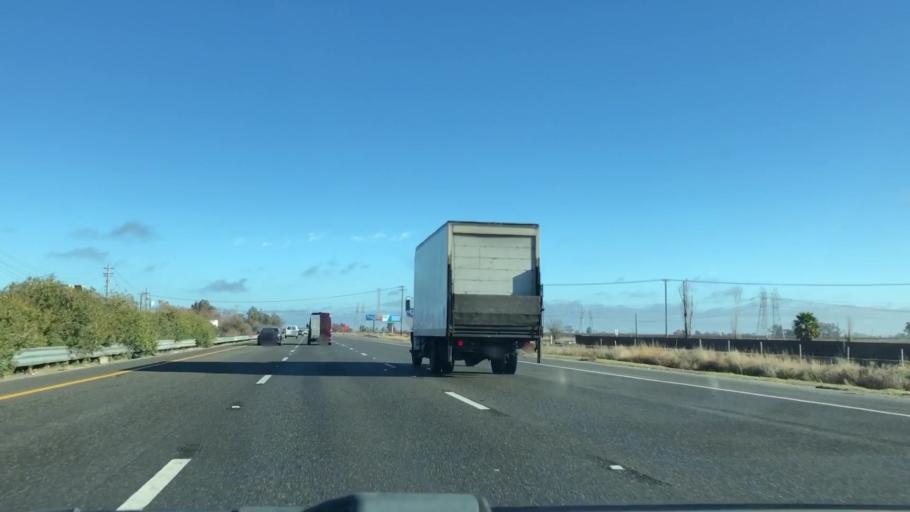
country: US
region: California
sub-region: Solano County
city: Hartley
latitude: 38.3926
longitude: -121.9255
